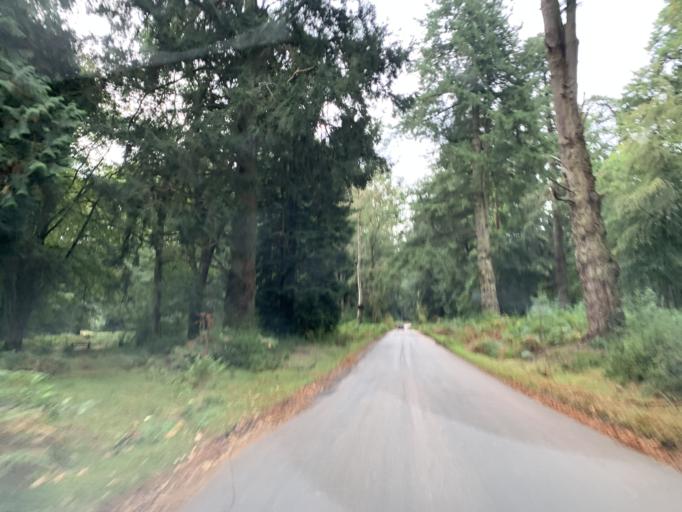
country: GB
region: England
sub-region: Hampshire
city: Lyndhurst
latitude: 50.8465
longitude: -1.6230
